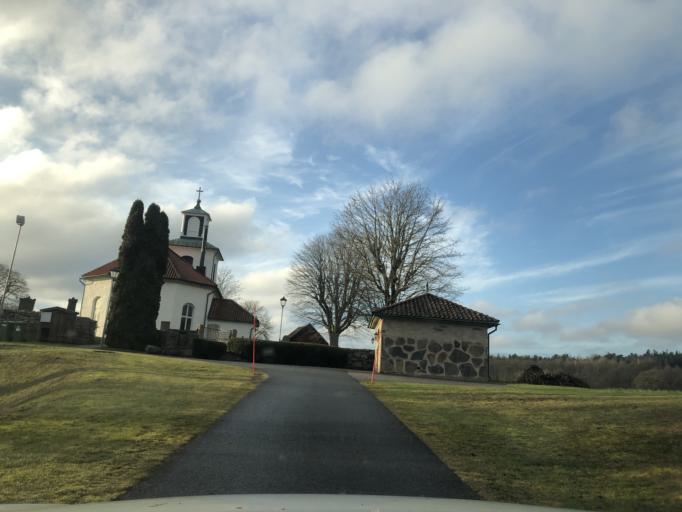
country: SE
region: Vaestra Goetaland
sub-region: Ulricehamns Kommun
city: Ulricehamn
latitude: 57.7440
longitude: 13.4166
